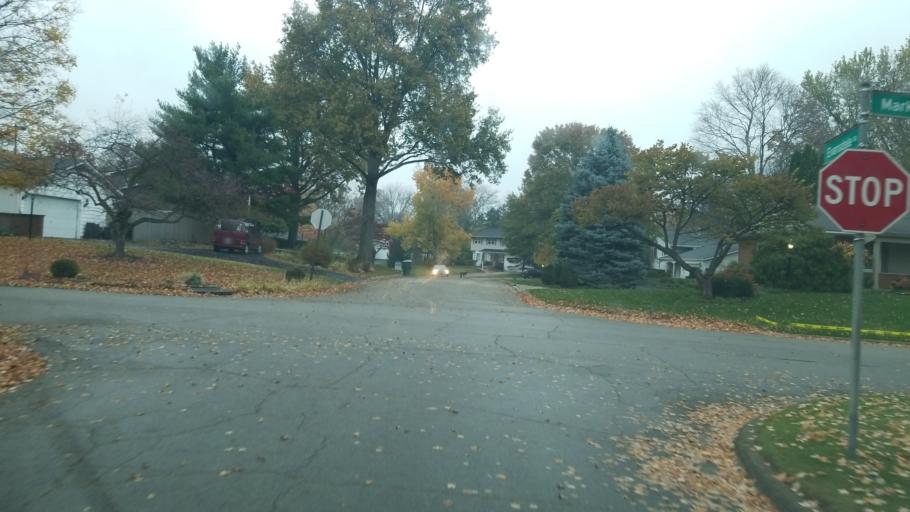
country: US
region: Ohio
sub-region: Franklin County
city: Worthington
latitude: 40.0468
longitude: -83.0353
